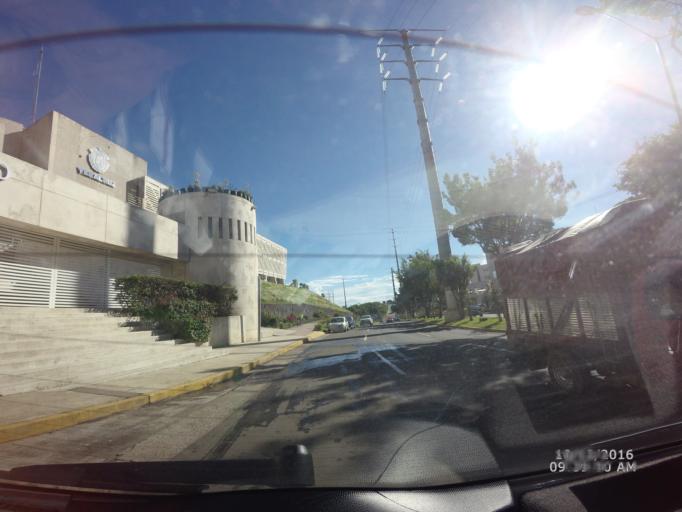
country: TR
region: Sivas
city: Karayun
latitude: 39.6694
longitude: 37.2933
